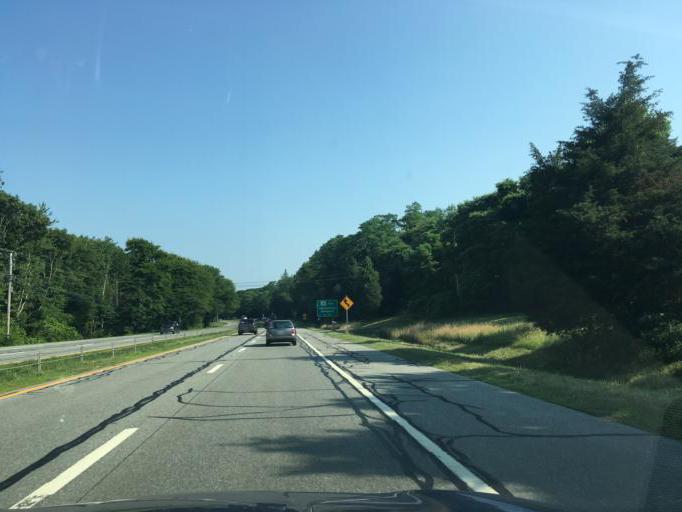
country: US
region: Rhode Island
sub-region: Washington County
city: North Kingstown
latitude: 41.5189
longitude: -71.4619
